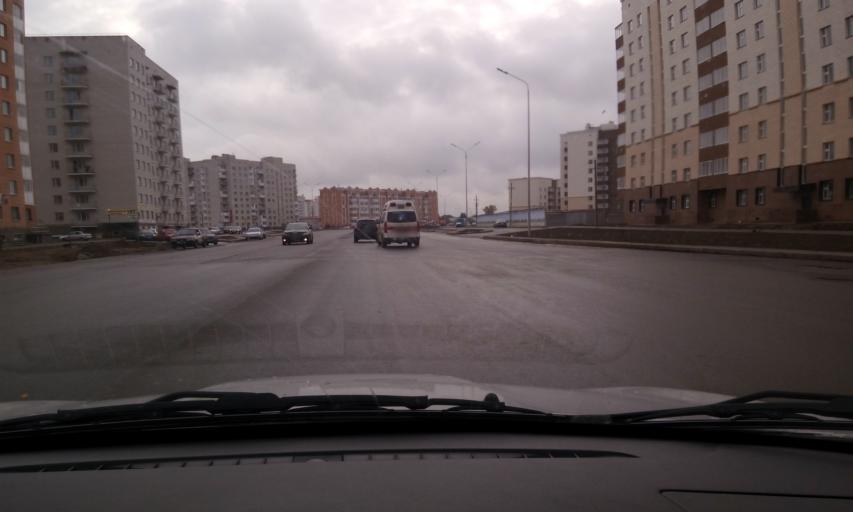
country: KZ
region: Astana Qalasy
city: Astana
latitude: 51.1266
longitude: 71.4990
